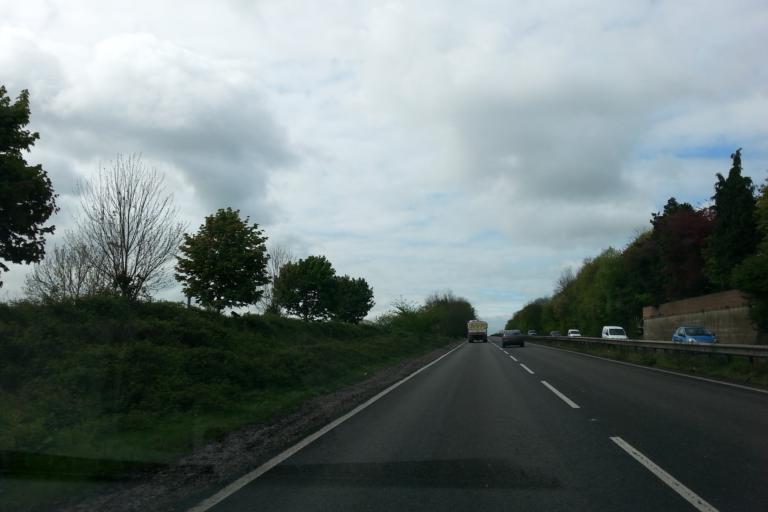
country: GB
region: England
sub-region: Staffordshire
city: Burton upon Trent
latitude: 52.8122
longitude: -1.6586
